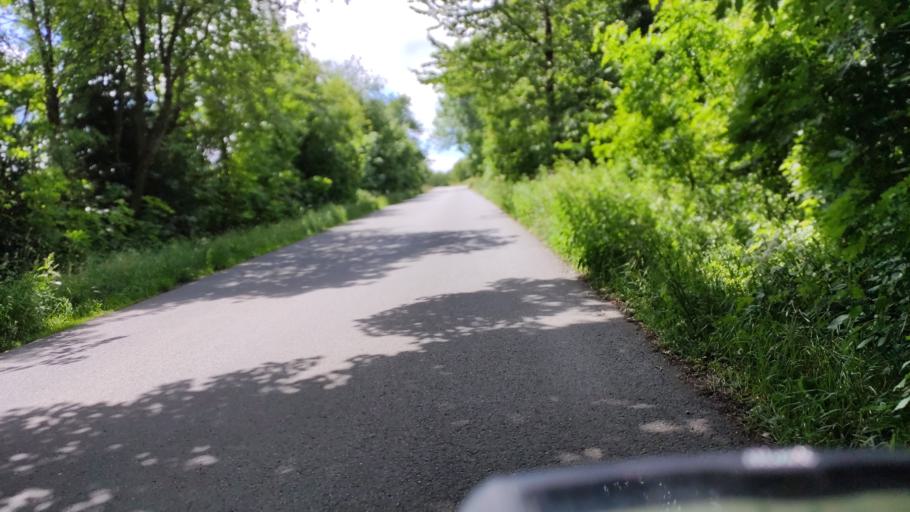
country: DE
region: Thuringia
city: Wurzbach
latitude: 50.4829
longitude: 11.5094
